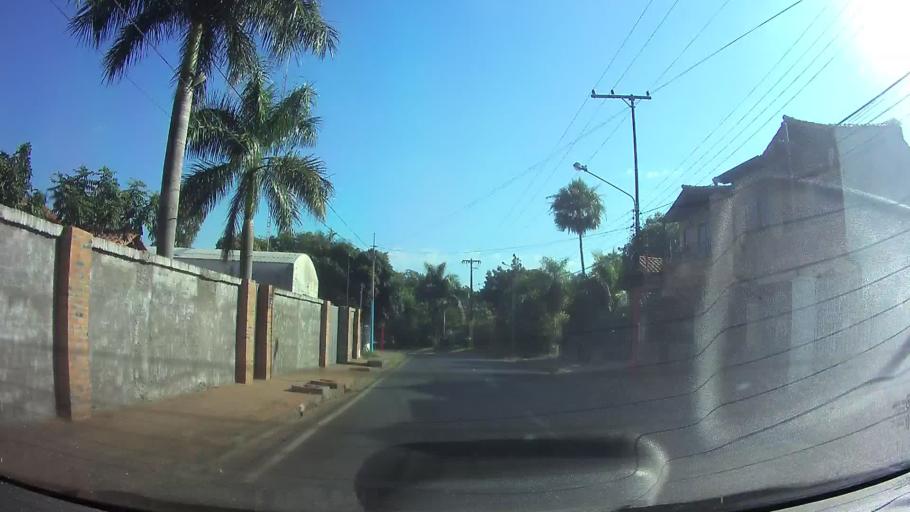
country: PY
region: Central
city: Fernando de la Mora
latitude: -25.2653
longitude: -57.5158
